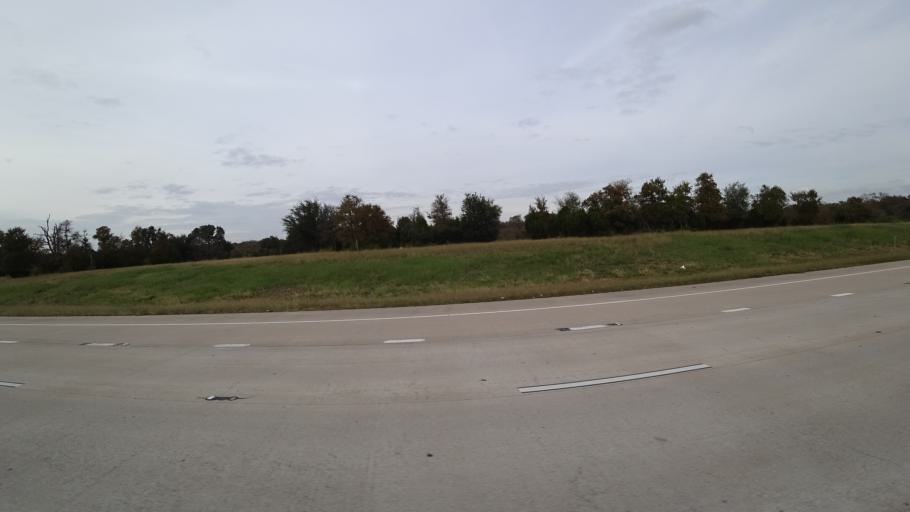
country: US
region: Texas
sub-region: Williamson County
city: Brushy Creek
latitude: 30.4778
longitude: -97.7282
